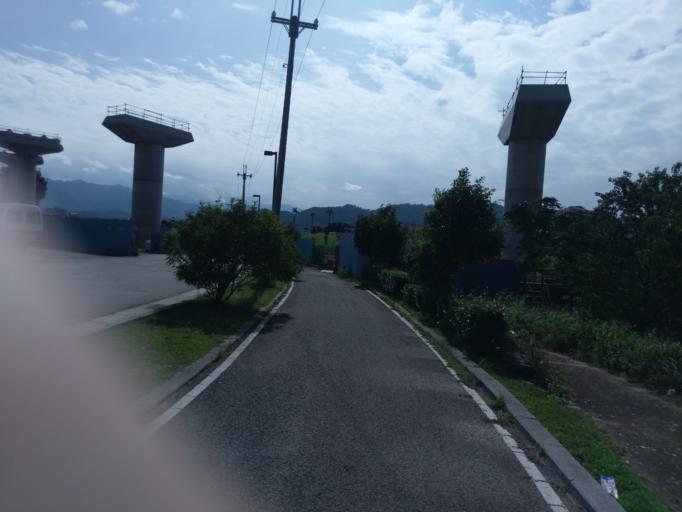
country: TW
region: Taiwan
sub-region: Taoyuan
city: Taoyuan
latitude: 24.9546
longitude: 121.3589
